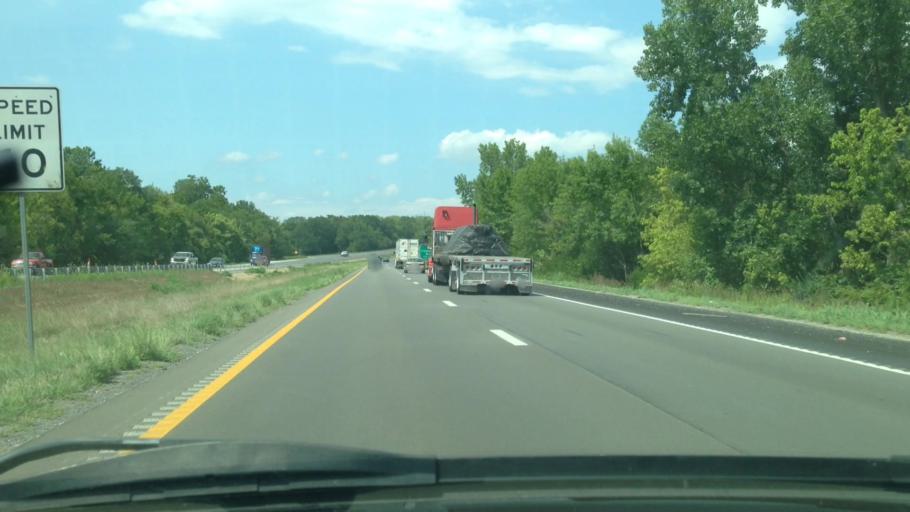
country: US
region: Missouri
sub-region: Lincoln County
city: Moscow Mills
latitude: 38.8888
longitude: -90.9190
